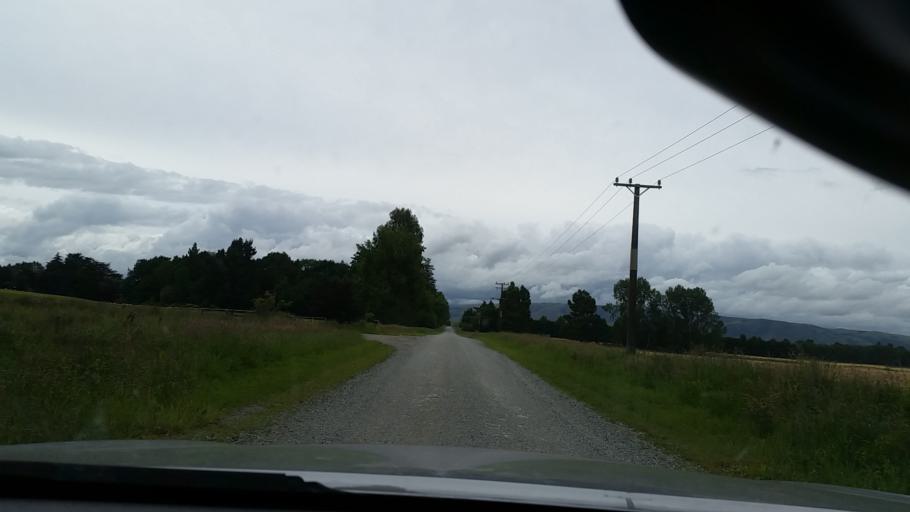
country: NZ
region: Otago
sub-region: Queenstown-Lakes District
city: Kingston
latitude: -45.7463
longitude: 168.7238
